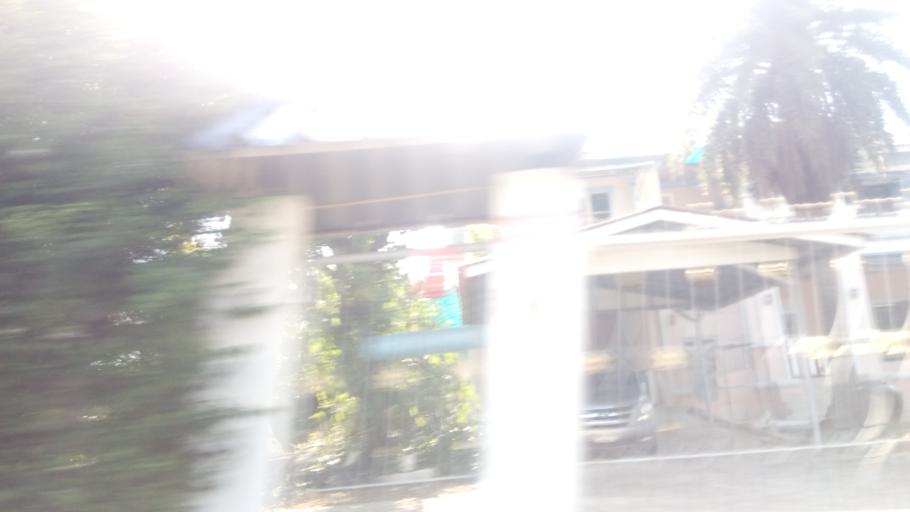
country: TH
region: Nakhon Pathom
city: Salaya
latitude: 13.8192
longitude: 100.3091
